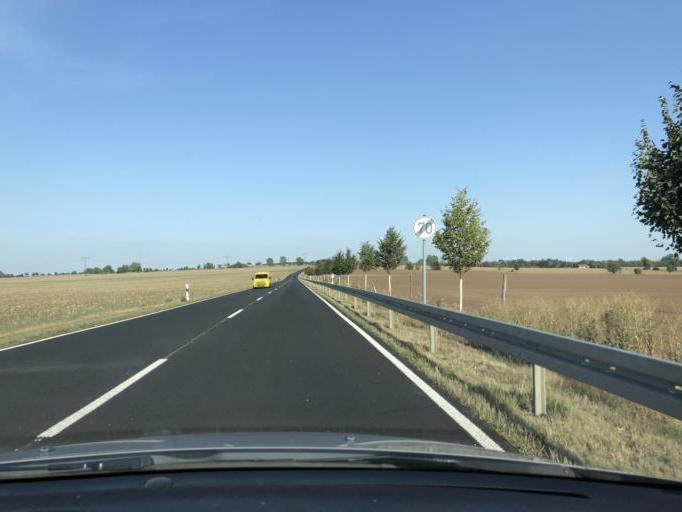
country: DE
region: Saxony-Anhalt
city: Braunsbedra
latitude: 51.2687
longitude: 11.8861
